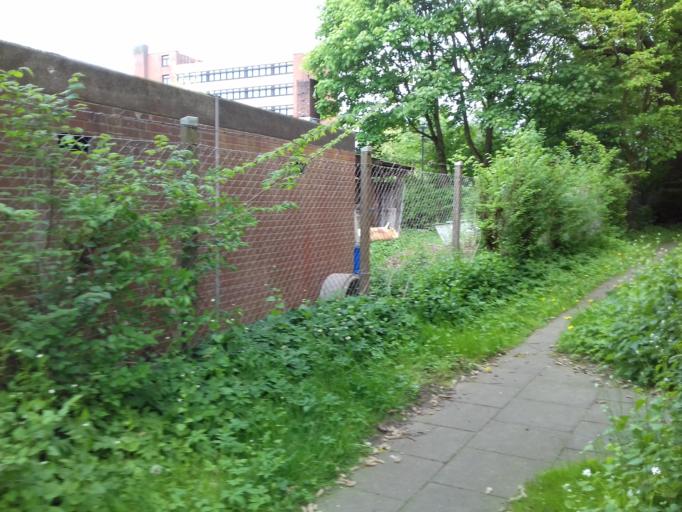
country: DE
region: Schleswig-Holstein
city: Rendsburg
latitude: 54.2965
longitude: 9.6689
